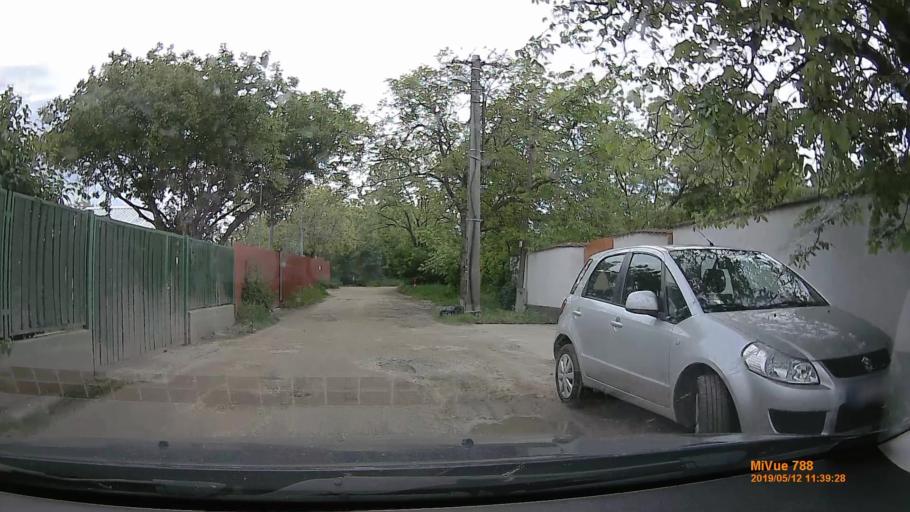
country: HU
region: Budapest
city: Budapest XVII. keruelet
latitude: 47.4648
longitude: 19.2580
